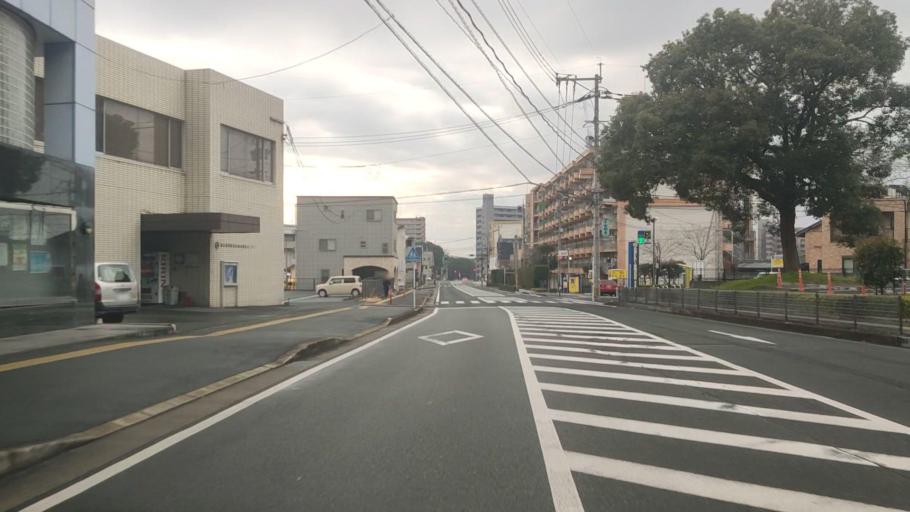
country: JP
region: Kumamoto
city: Kumamoto
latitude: 32.7908
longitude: 130.7400
